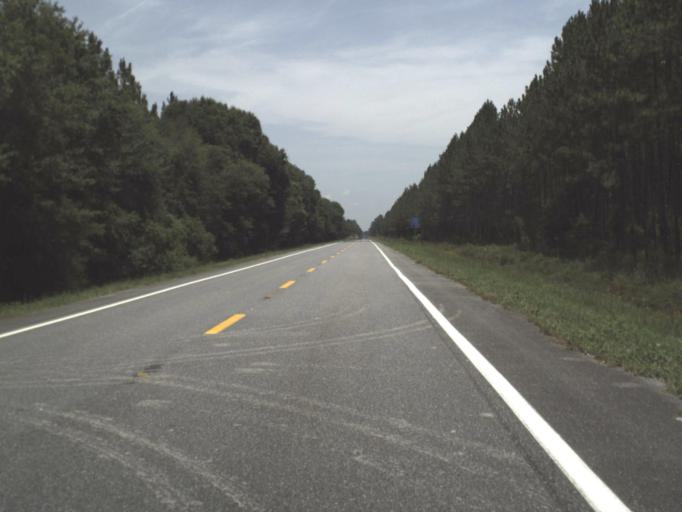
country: US
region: Florida
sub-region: Taylor County
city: Steinhatchee
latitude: 29.8233
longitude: -83.3153
